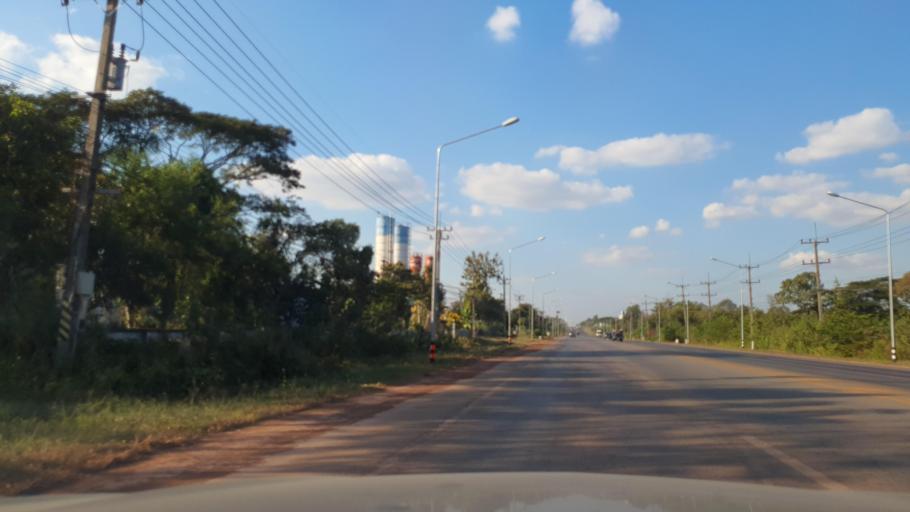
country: TH
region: Sakon Nakhon
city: Sakon Nakhon
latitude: 17.1565
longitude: 104.1046
